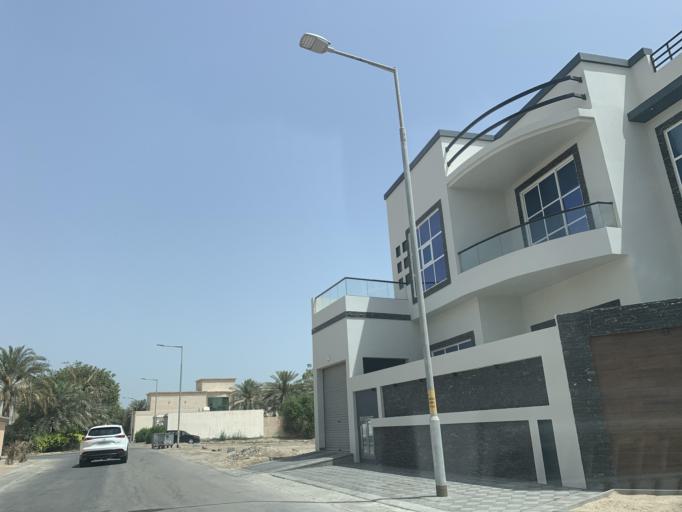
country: BH
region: Northern
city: Sitrah
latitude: 26.1570
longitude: 50.5854
